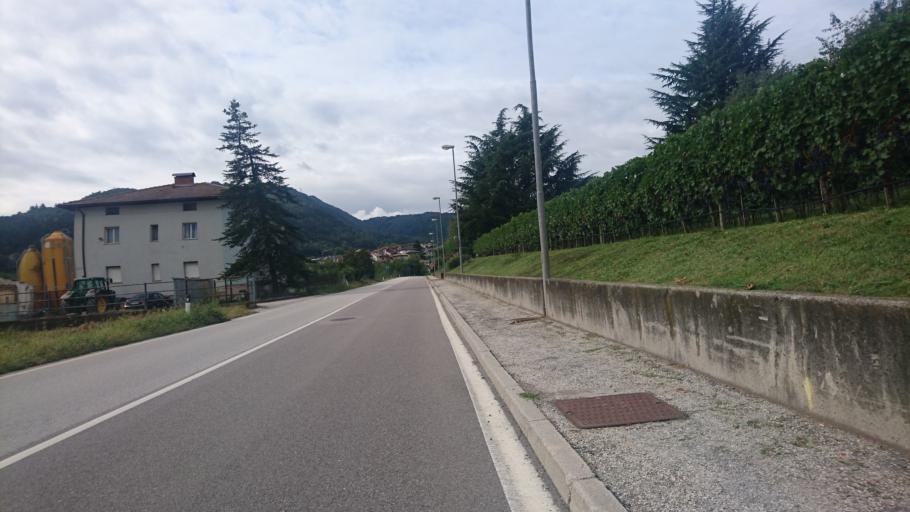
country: IT
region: Trentino-Alto Adige
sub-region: Provincia di Trento
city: Civezzano
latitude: 46.0871
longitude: 11.1892
